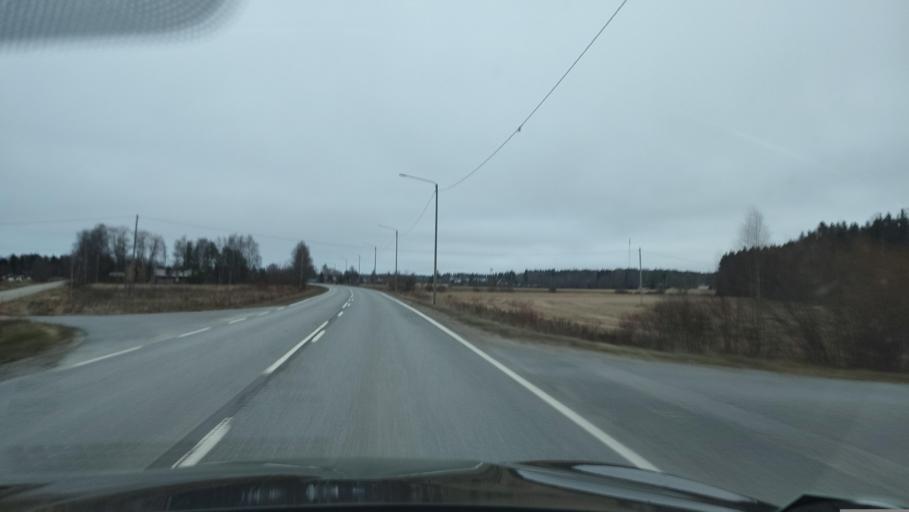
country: FI
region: Southern Ostrobothnia
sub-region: Suupohja
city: Kauhajoki
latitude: 62.3505
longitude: 22.0507
